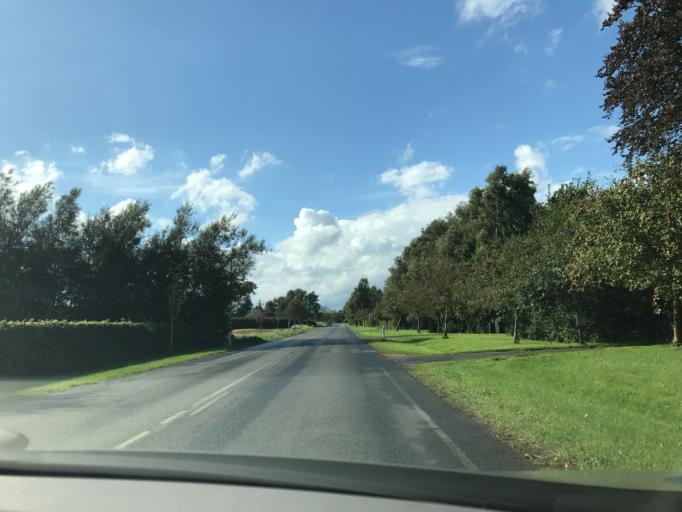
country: DK
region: South Denmark
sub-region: Middelfart Kommune
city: Strib
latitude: 55.5025
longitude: 9.7952
